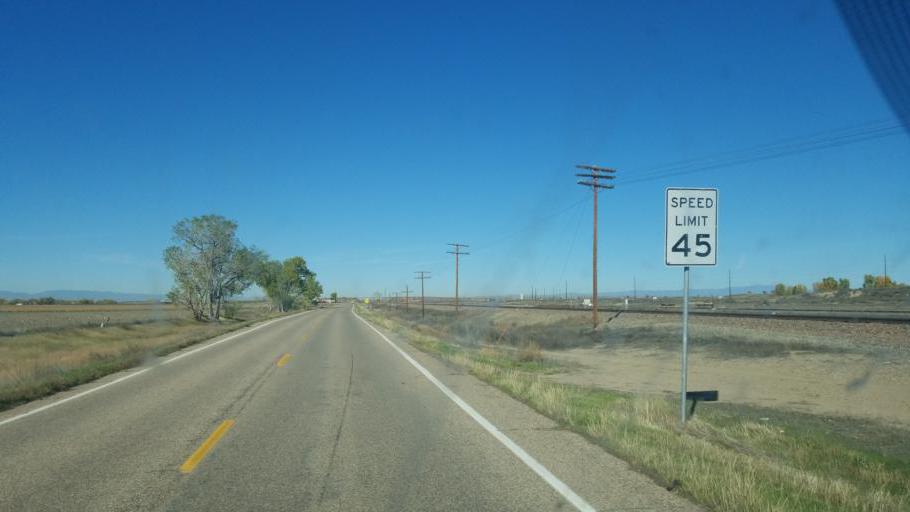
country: US
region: Colorado
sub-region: Pueblo County
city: Pueblo
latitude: 38.2628
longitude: -104.3536
